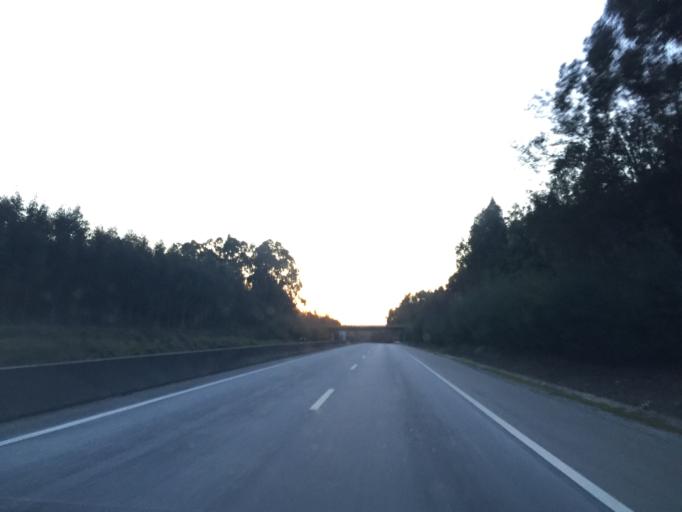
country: PT
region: Viseu
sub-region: Concelho de Carregal do Sal
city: Carregal do Sal
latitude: 40.4163
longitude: -8.0441
